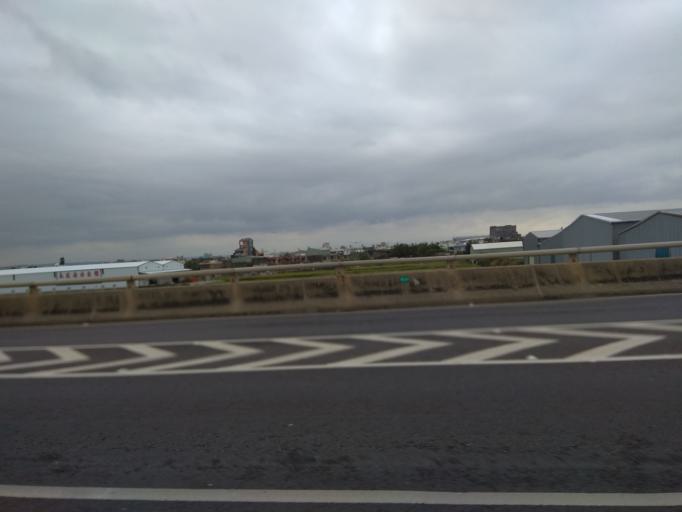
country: TW
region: Taiwan
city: Taoyuan City
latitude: 25.0871
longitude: 121.1857
